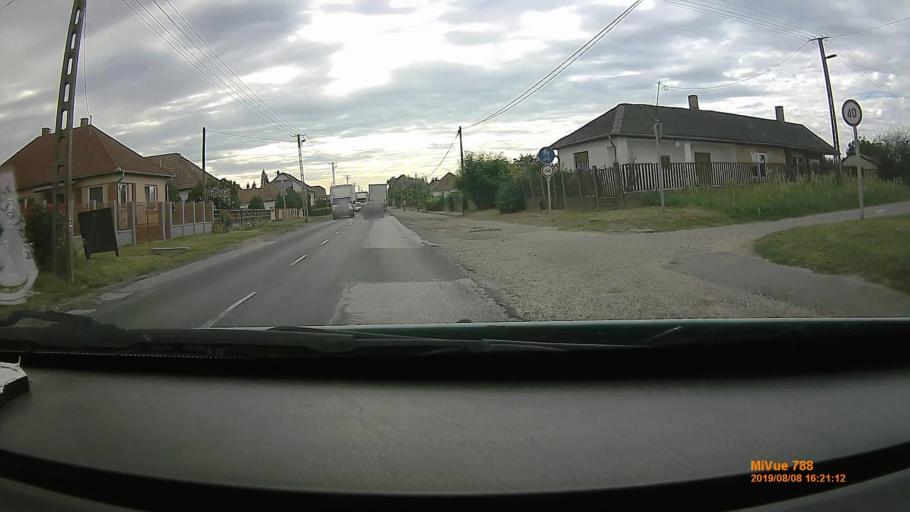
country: HU
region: Szabolcs-Szatmar-Bereg
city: Nyirmeggyes
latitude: 47.9686
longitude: 22.2615
